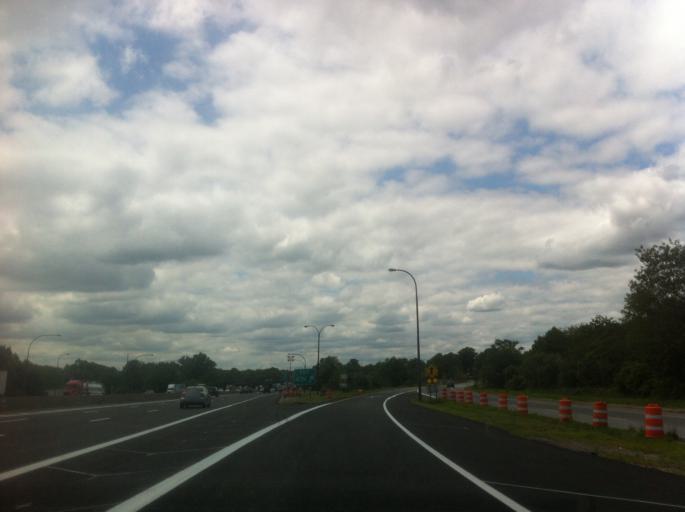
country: US
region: New York
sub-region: Nassau County
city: Jericho
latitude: 40.7870
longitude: -73.5274
